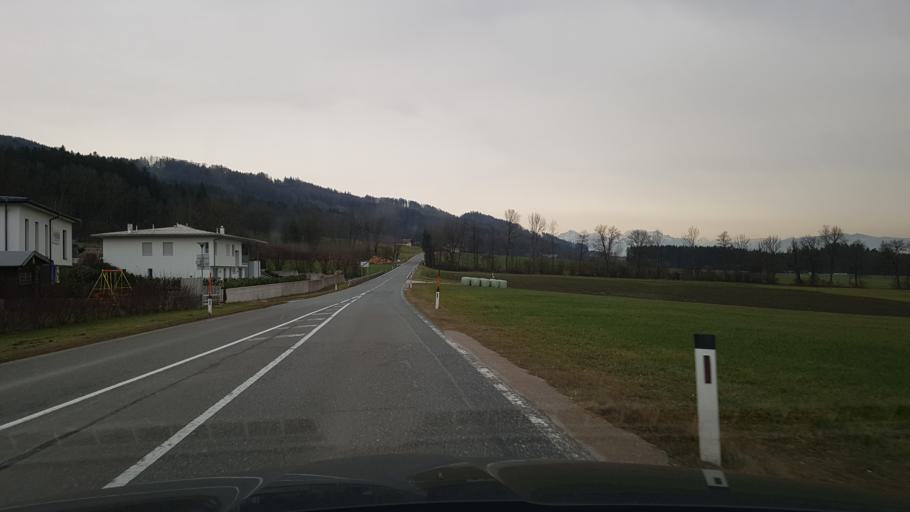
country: AT
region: Salzburg
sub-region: Politischer Bezirk Salzburg-Umgebung
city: Nussdorf am Haunsberg
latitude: 47.9480
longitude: 13.0018
